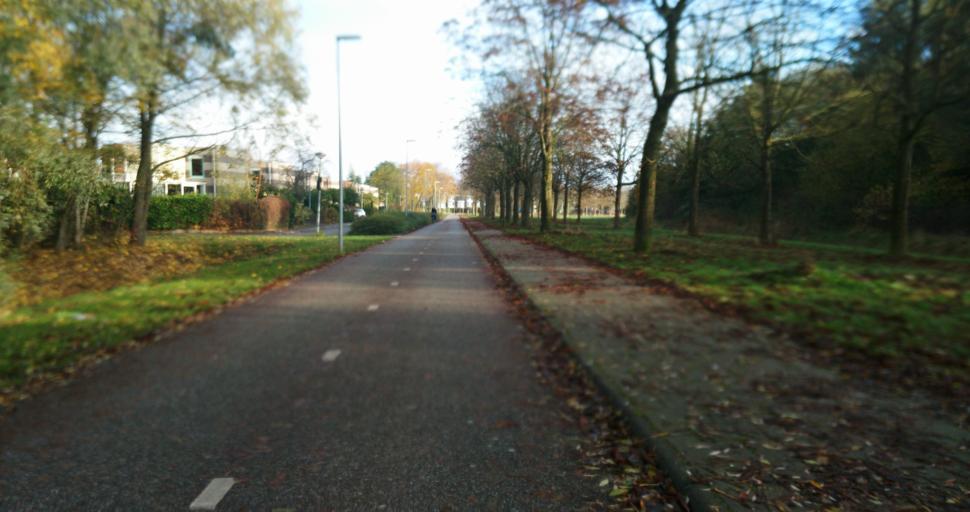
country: NL
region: Groningen
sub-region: Gemeente Groningen
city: Korrewegwijk
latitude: 53.2379
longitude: 6.5798
